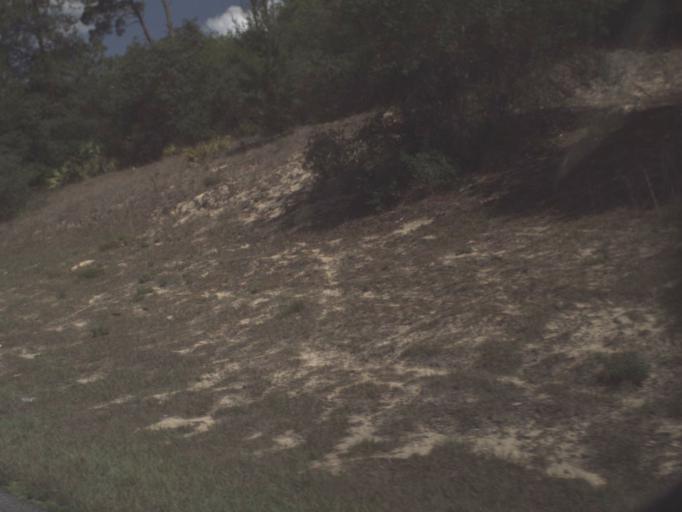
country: US
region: Florida
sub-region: Lake County
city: Astor
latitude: 29.1671
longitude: -81.6503
